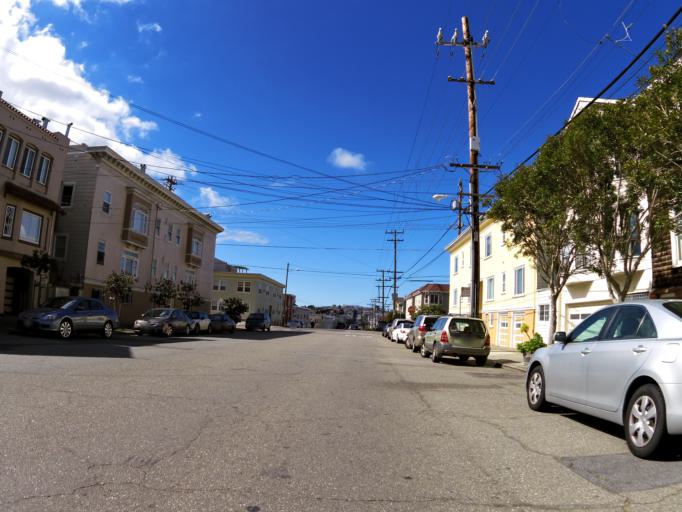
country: US
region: California
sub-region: San Francisco County
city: San Francisco
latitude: 37.7787
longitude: -122.4743
